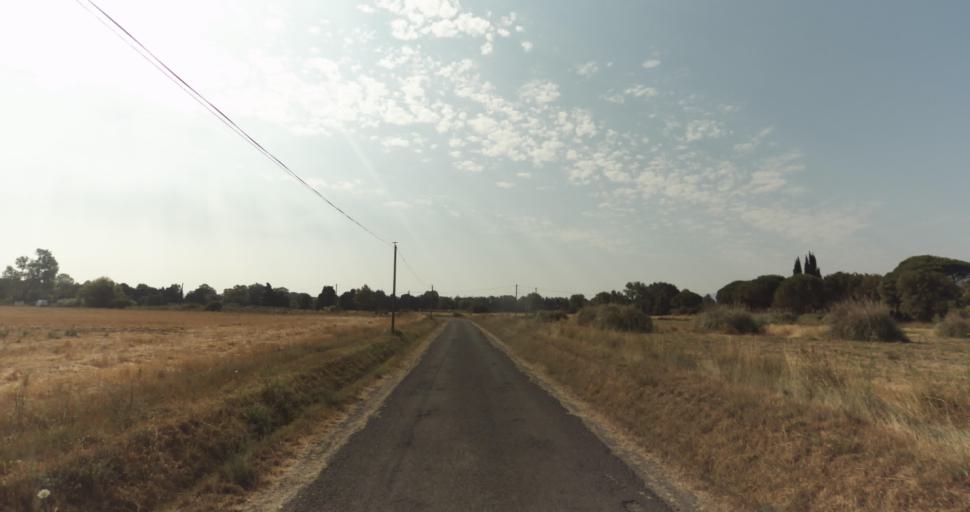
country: FR
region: Languedoc-Roussillon
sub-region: Departement des Pyrenees-Orientales
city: Latour-Bas-Elne
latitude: 42.6122
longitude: 3.0160
